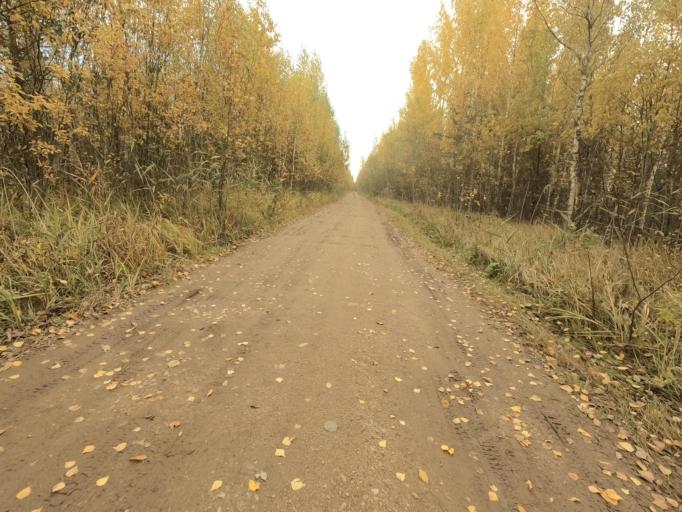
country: RU
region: Novgorod
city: Pankovka
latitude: 58.8765
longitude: 30.8693
